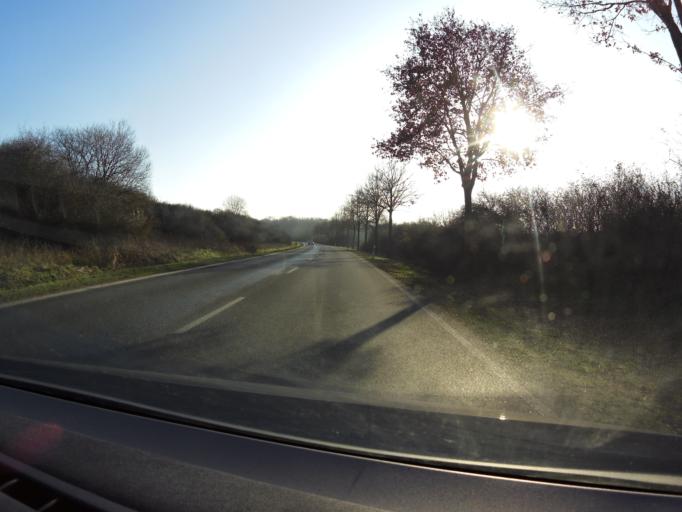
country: DE
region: North Rhine-Westphalia
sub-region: Regierungsbezirk Dusseldorf
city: Bruggen
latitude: 51.2743
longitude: 6.1822
